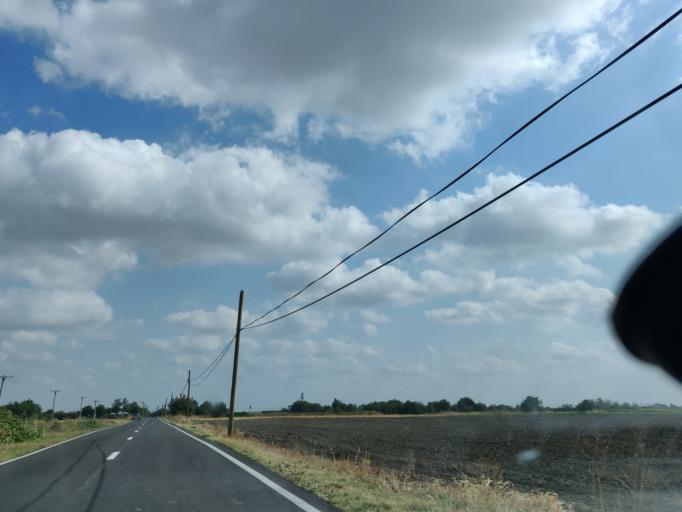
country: RO
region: Vrancea
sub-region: Comuna Ciorasti
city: Ciorasti
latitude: 45.4246
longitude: 27.2854
